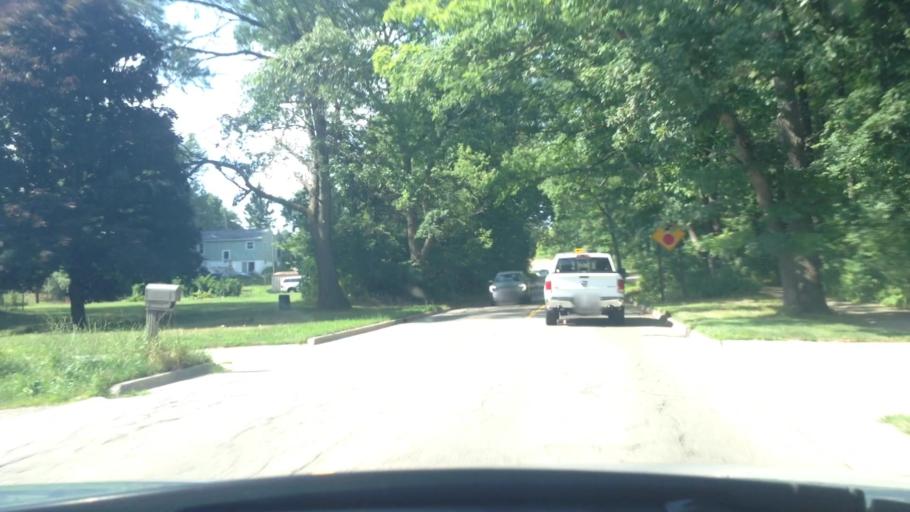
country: US
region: Michigan
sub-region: Oakland County
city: Clarkston
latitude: 42.7512
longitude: -83.3507
